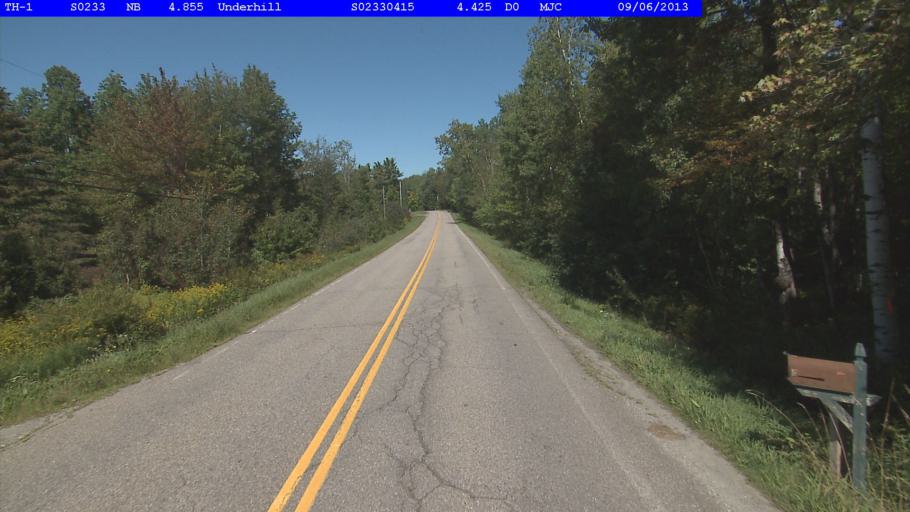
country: US
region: Vermont
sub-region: Chittenden County
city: Jericho
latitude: 44.5301
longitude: -72.8761
